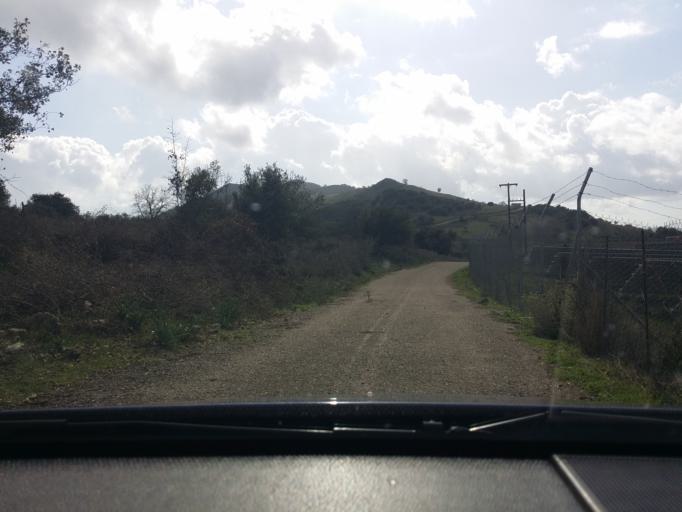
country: GR
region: West Greece
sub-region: Nomos Aitolias kai Akarnanias
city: Fitiai
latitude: 38.6711
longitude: 21.1902
